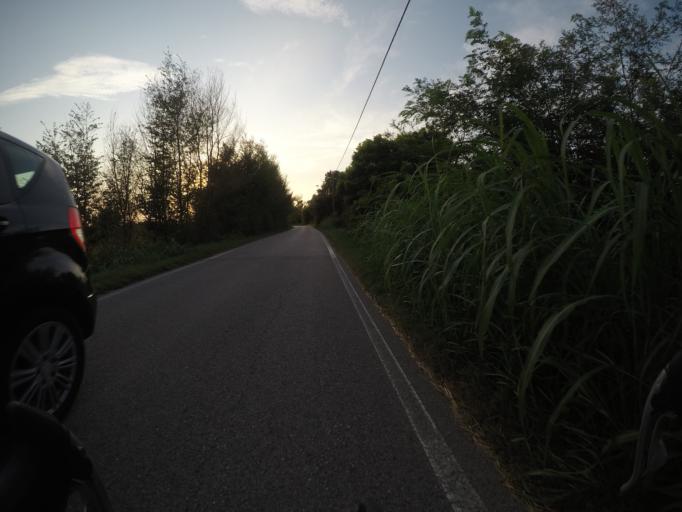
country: IT
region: Veneto
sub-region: Provincia di Rovigo
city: Pincara
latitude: 45.0028
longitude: 11.6158
